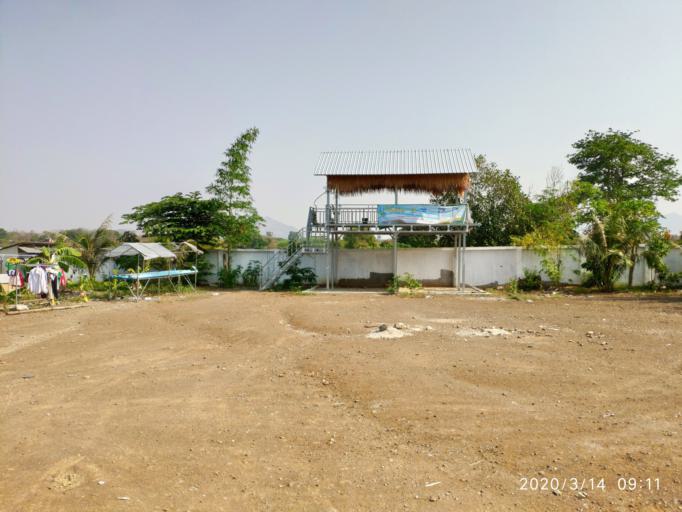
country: KH
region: Pailin
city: Pailin
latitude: 12.8454
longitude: 102.6184
